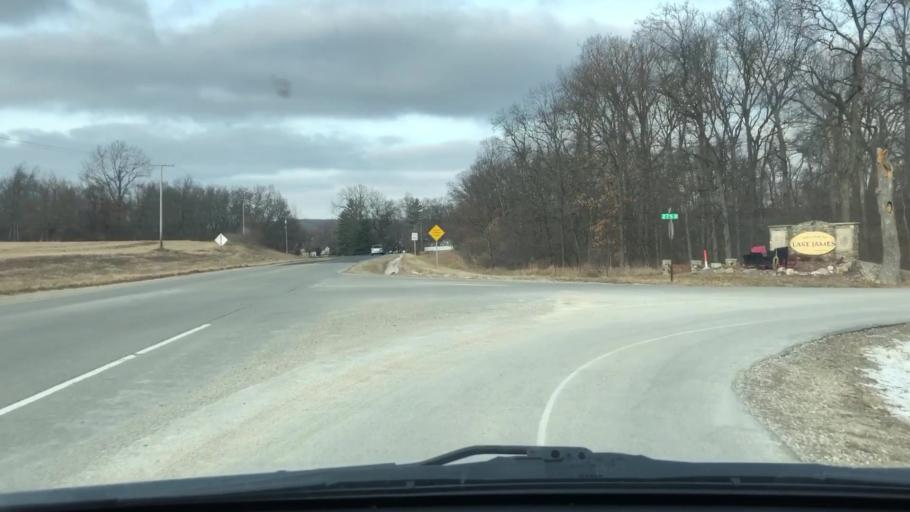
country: US
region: Indiana
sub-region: Steuben County
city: Angola
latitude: 41.6807
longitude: -85.0287
